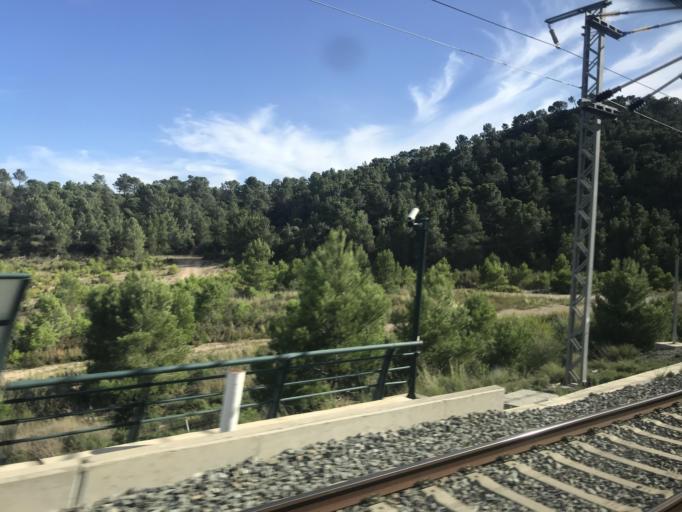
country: ES
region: Catalonia
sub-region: Provincia de Tarragona
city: l'Ametlla de Mar
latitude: 40.9781
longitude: 0.8924
